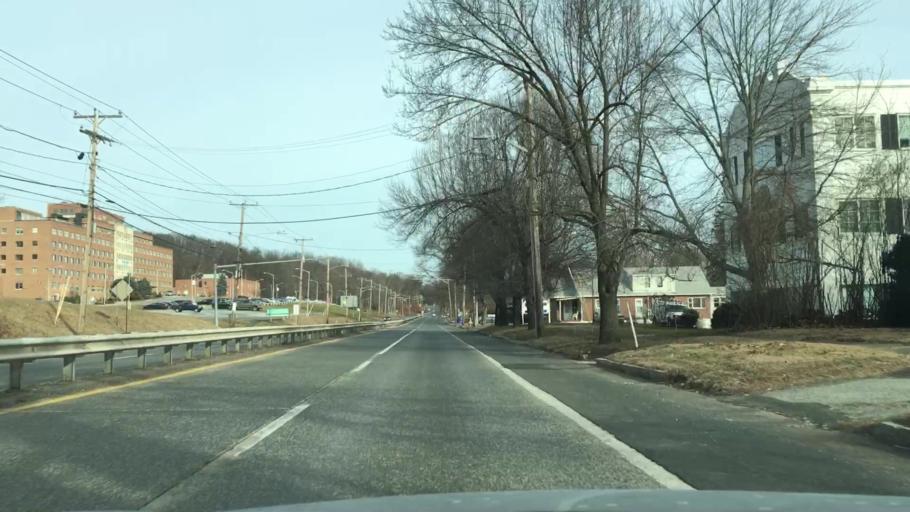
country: US
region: Massachusetts
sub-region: Hampden County
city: Chicopee
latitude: 42.1634
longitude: -72.6329
